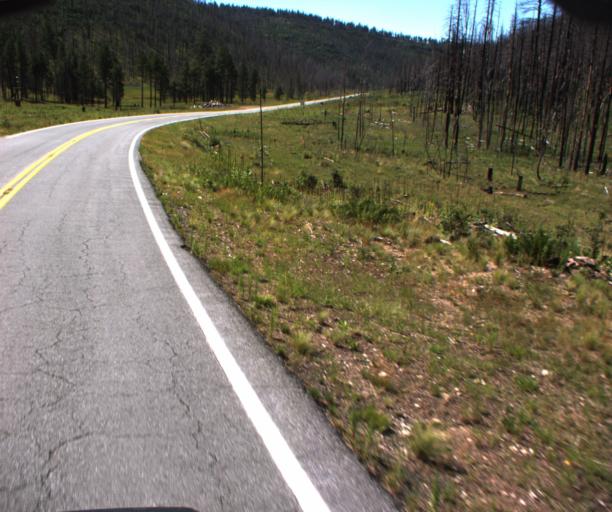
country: US
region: Arizona
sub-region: Apache County
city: Eagar
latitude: 33.8058
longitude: -109.1548
